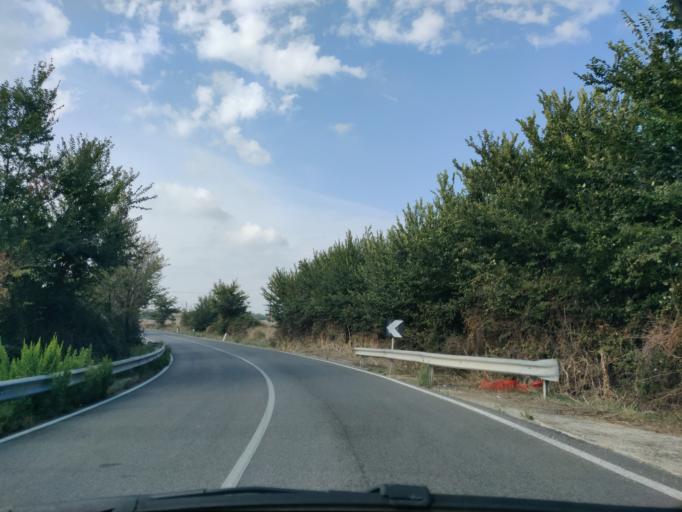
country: IT
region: Latium
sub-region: Provincia di Viterbo
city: Tarquinia
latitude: 42.2288
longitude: 11.7978
